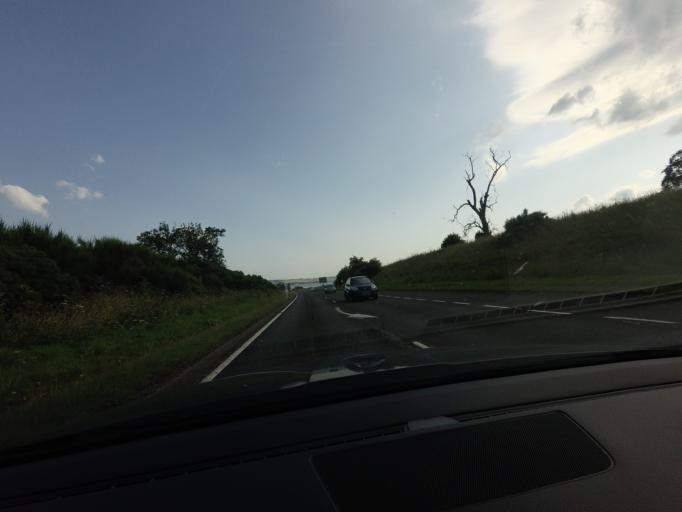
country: GB
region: Scotland
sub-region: Highland
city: Evanton
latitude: 57.6504
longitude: -4.3398
